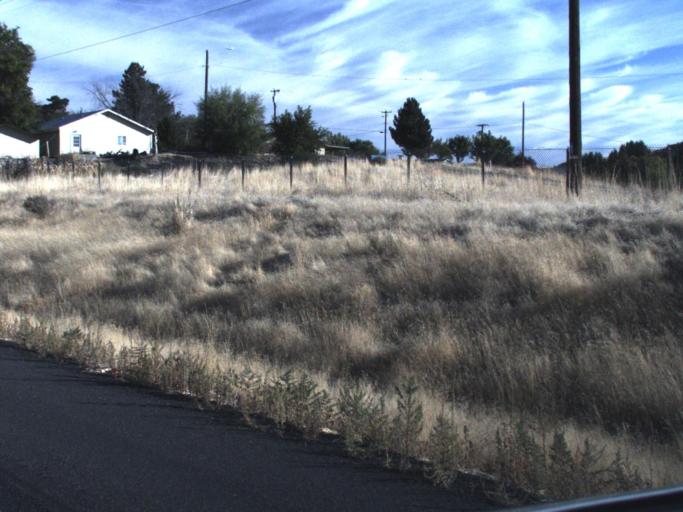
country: US
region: Washington
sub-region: Franklin County
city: Basin City
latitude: 46.5774
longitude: -119.0040
